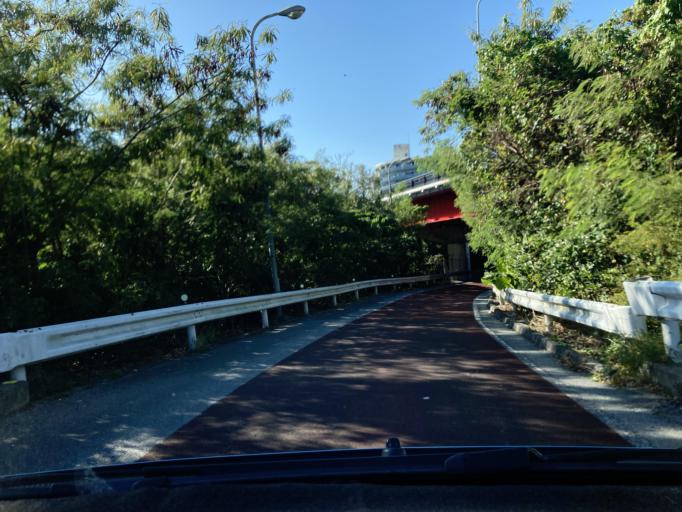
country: JP
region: Okinawa
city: Ginowan
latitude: 26.2554
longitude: 127.7294
